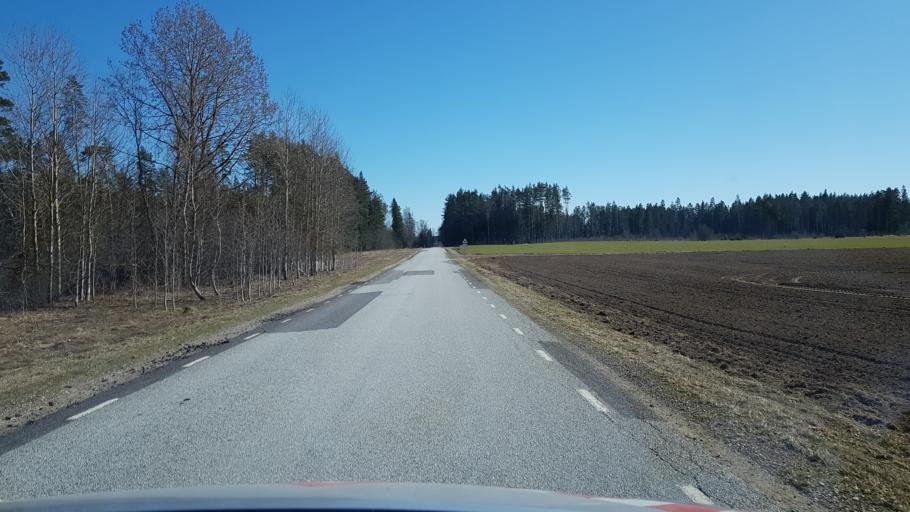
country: EE
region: Laeaene-Virumaa
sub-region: Viru-Nigula vald
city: Kunda
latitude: 59.3850
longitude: 26.5733
